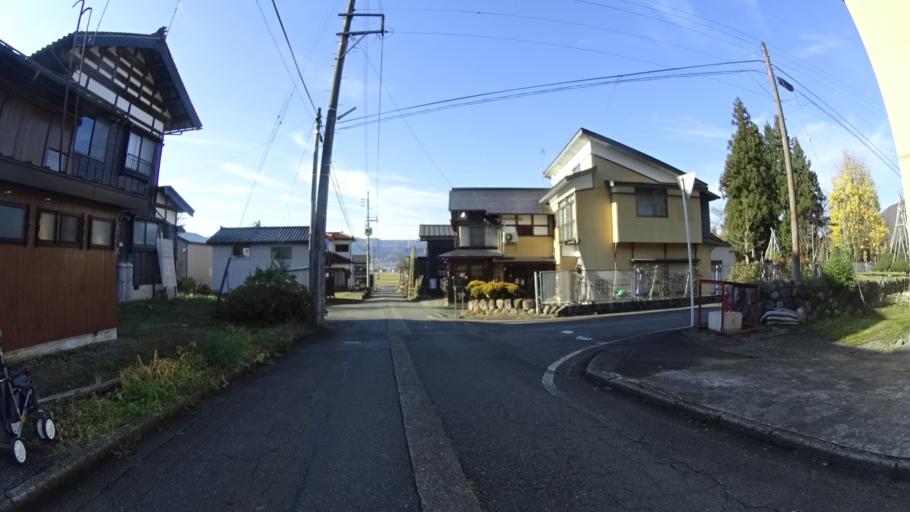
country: JP
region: Niigata
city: Muikamachi
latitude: 37.0321
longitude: 138.8887
